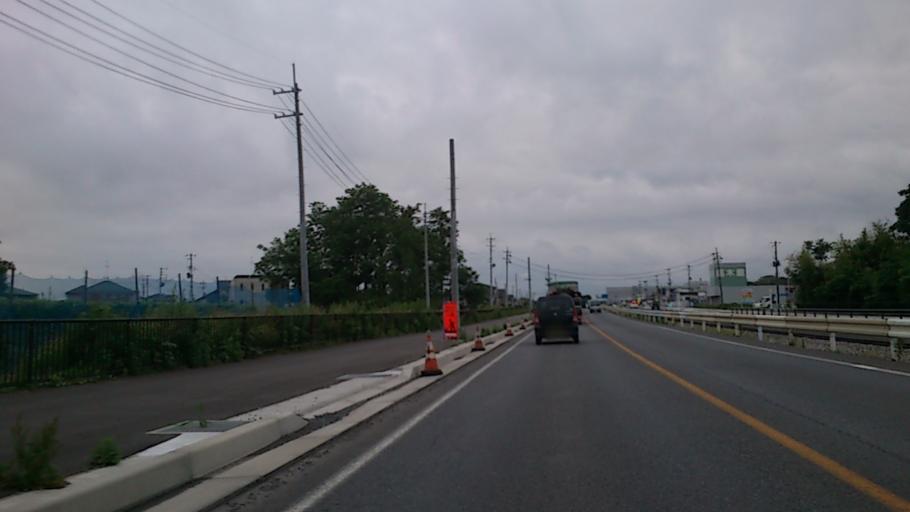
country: JP
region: Fukushima
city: Sukagawa
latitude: 37.2595
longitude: 140.3473
